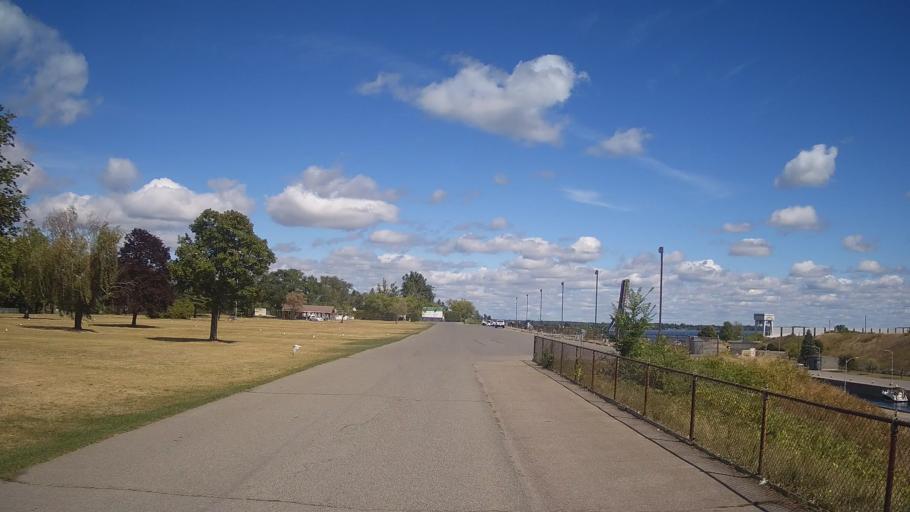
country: US
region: New York
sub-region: St. Lawrence County
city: Ogdensburg
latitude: 44.8300
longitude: -75.3144
